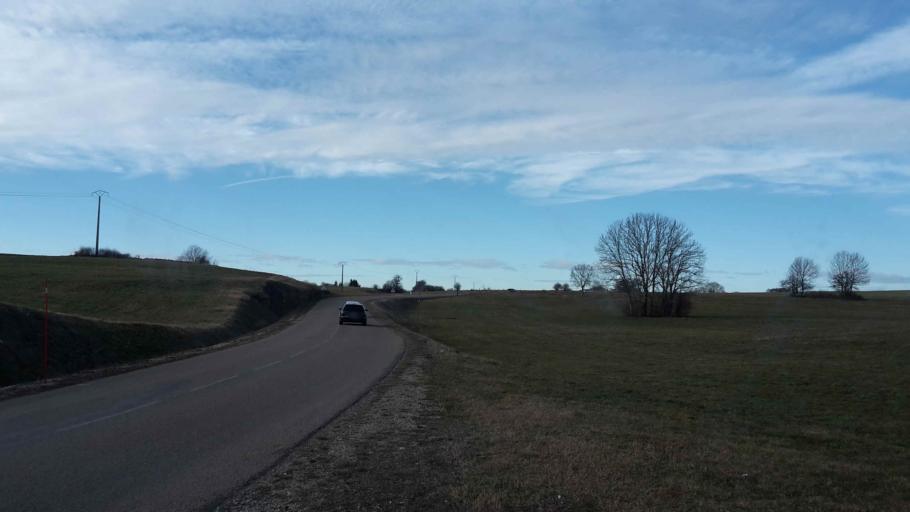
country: FR
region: Franche-Comte
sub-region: Departement du Doubs
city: Valdahon
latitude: 47.1126
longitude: 6.3603
